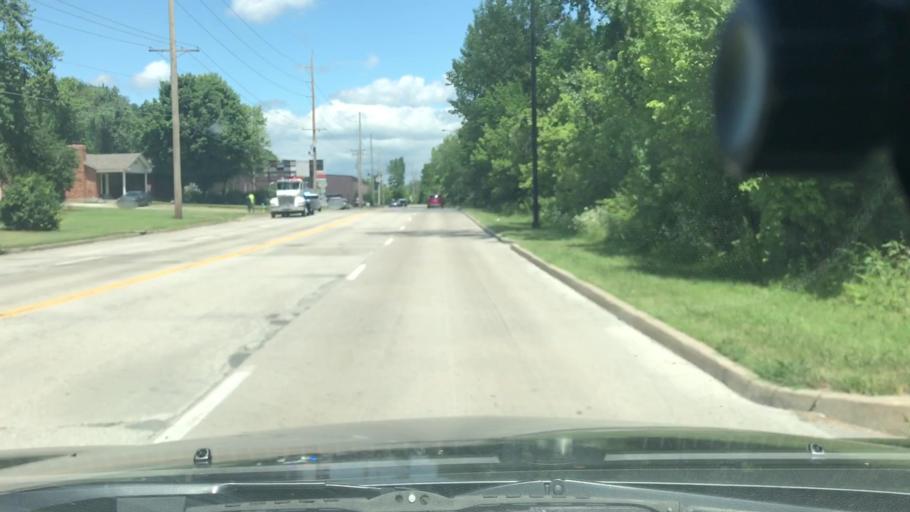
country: US
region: Missouri
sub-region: Saint Charles County
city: Saint Charles
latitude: 38.7591
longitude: -90.4969
